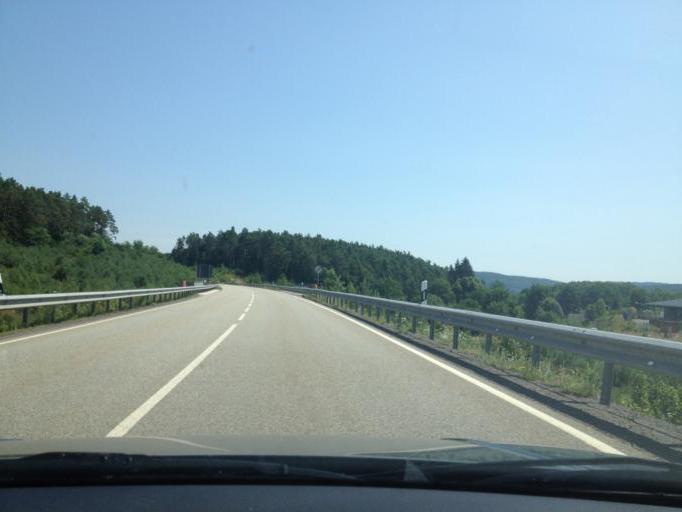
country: DE
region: Rheinland-Pfalz
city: Hochspeyer
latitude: 49.4423
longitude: 7.8725
